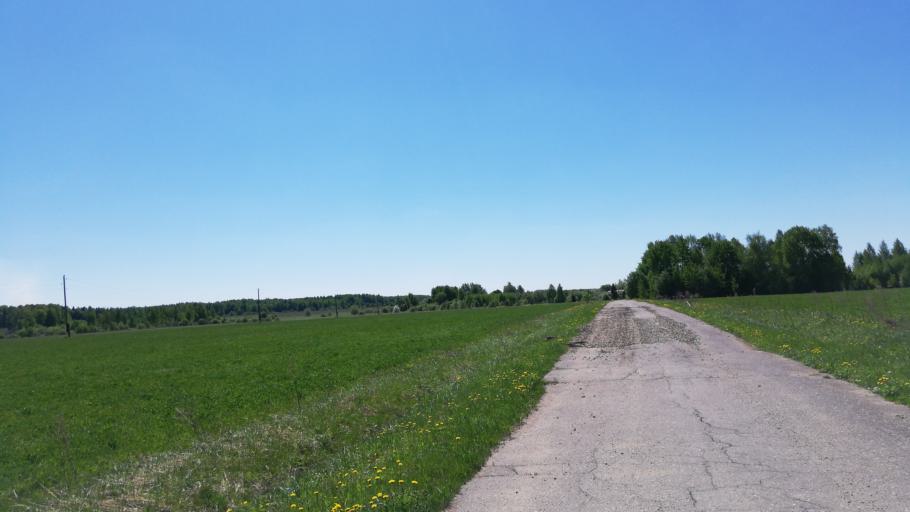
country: RU
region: Ivanovo
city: Pistsovo
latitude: 57.1216
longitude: 40.5990
